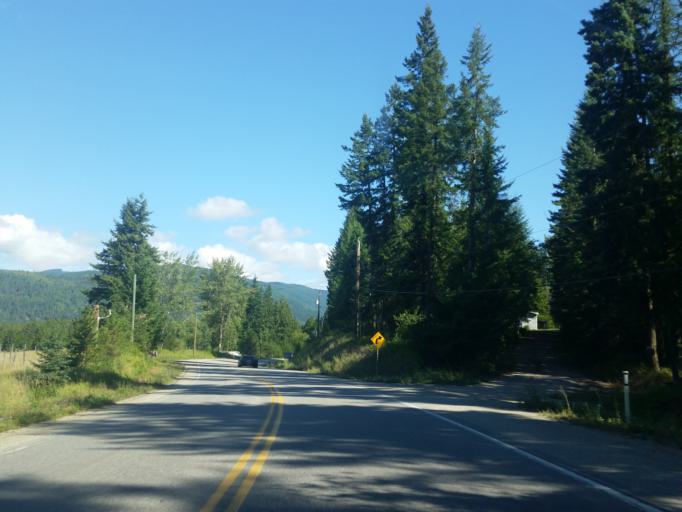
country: CA
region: British Columbia
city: Sicamous
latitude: 50.6925
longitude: -119.0420
